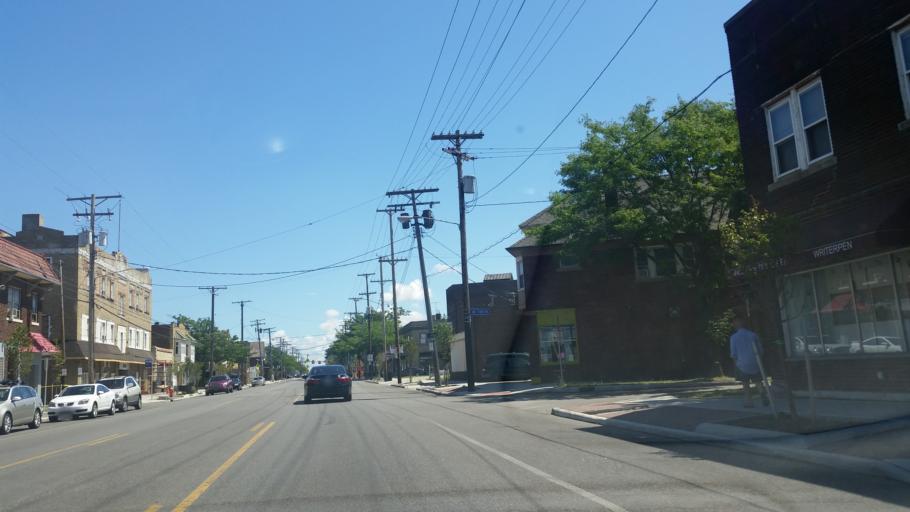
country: US
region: Ohio
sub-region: Cuyahoga County
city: Lakewood
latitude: 41.4608
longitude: -81.7723
